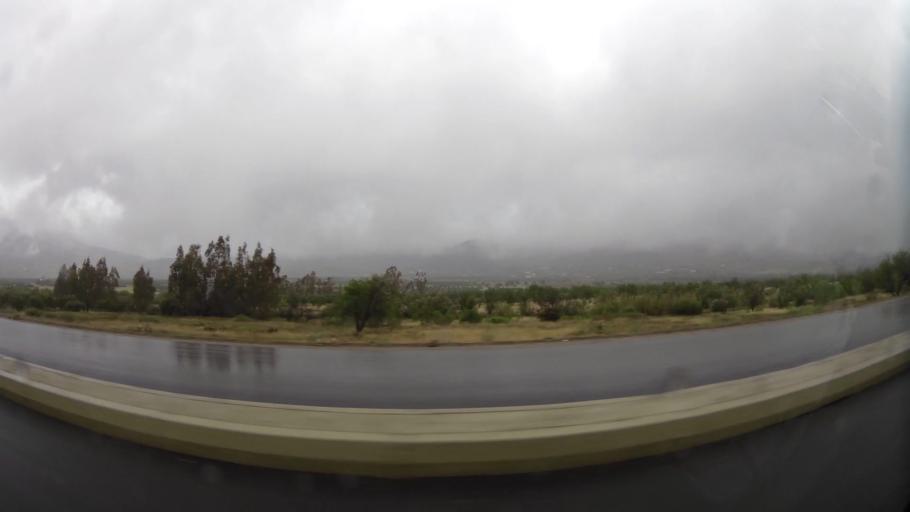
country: MA
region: Oriental
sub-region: Nador
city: Midar
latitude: 34.8256
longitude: -3.7219
